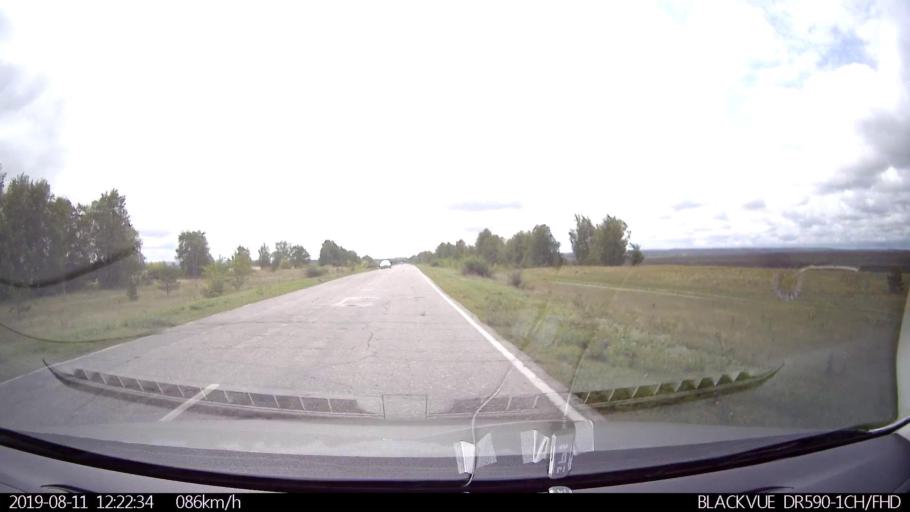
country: RU
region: Ulyanovsk
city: Ignatovka
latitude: 53.9058
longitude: 47.9528
